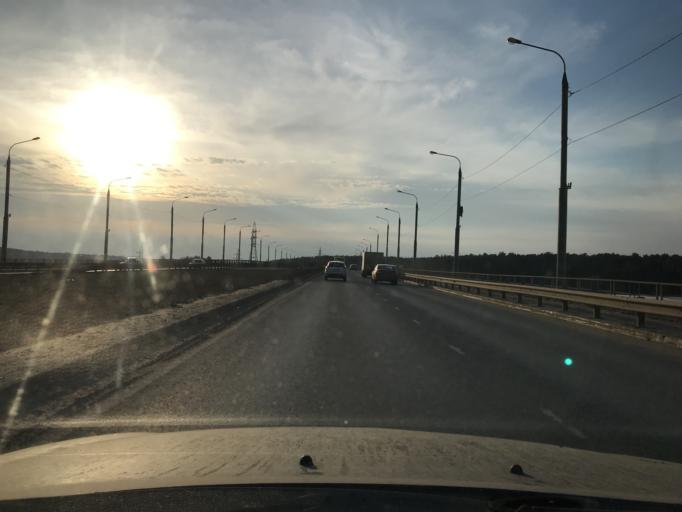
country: RU
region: Kaluga
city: Kaluga
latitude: 54.5116
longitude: 36.2185
